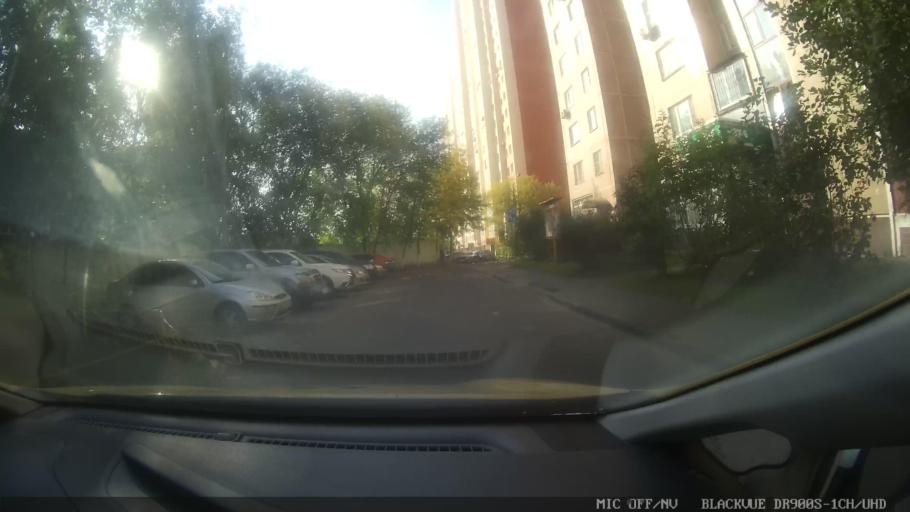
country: RU
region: Moskovskaya
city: Reutov
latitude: 55.7508
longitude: 37.8766
